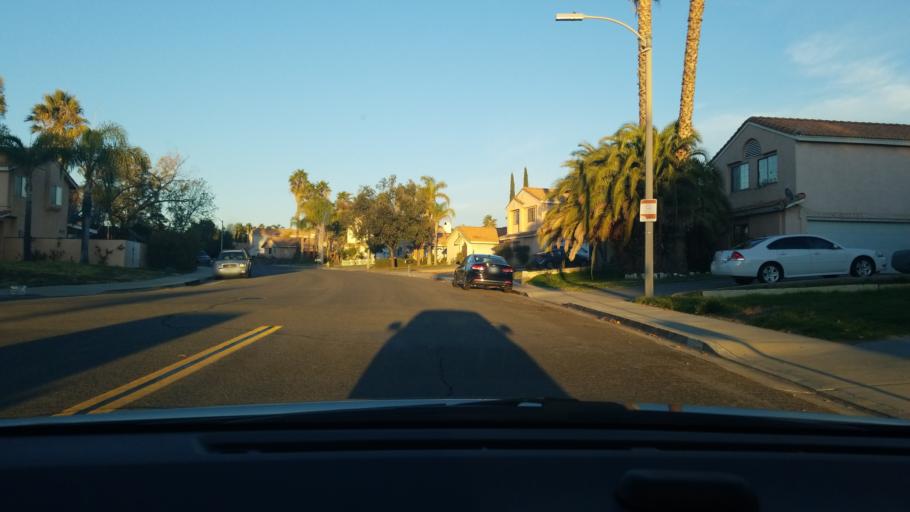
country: US
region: California
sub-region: Riverside County
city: Murrieta Hot Springs
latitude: 33.5418
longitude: -117.1504
